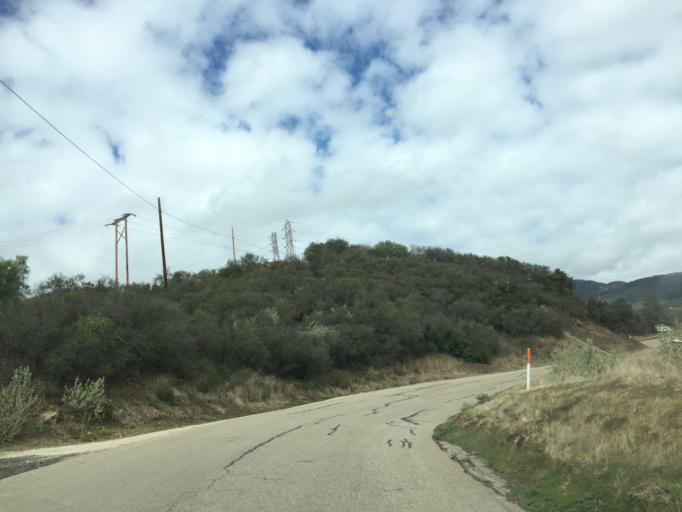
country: US
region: California
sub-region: Santa Barbara County
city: Goleta
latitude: 34.4741
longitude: -119.7999
